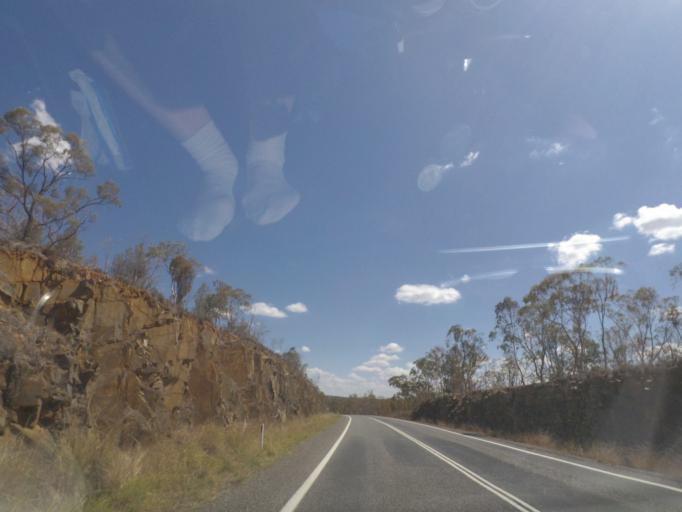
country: AU
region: Queensland
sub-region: Southern Downs
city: Warwick
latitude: -28.2098
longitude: 151.5651
